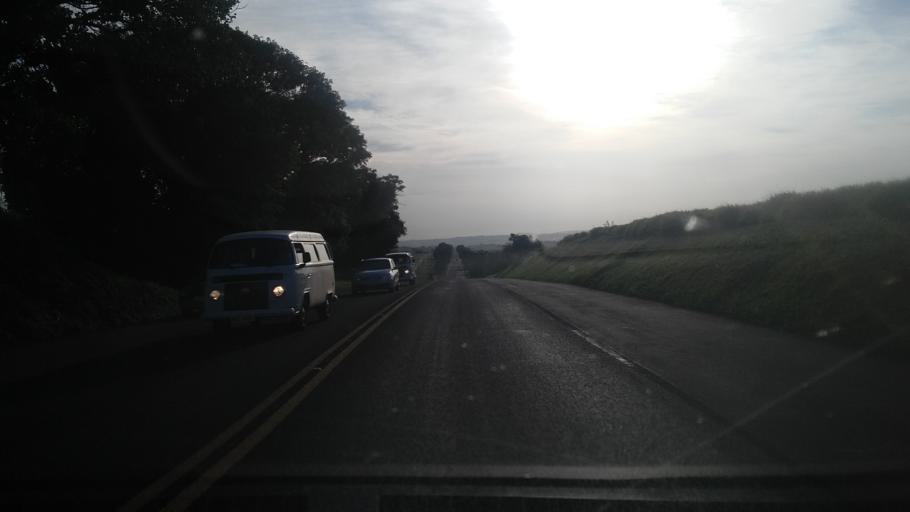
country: BR
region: Parana
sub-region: Bandeirantes
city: Bandeirantes
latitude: -23.1479
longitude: -50.5475
